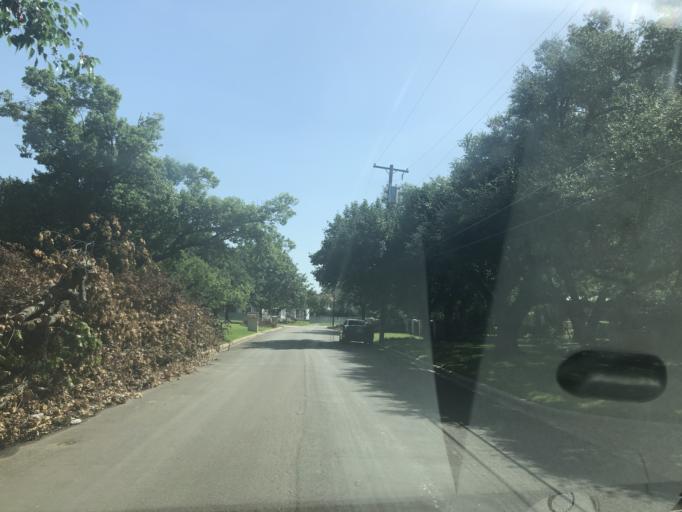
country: US
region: Texas
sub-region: Dallas County
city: University Park
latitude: 32.8831
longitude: -96.8176
